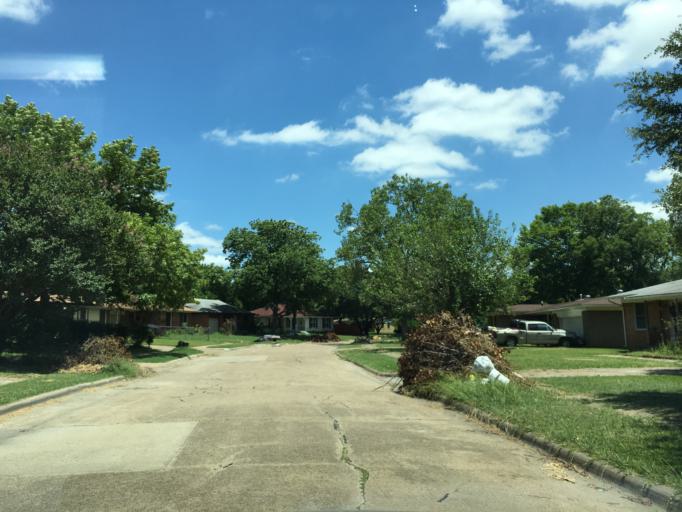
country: US
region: Texas
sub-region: Dallas County
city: Garland
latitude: 32.8379
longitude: -96.6671
